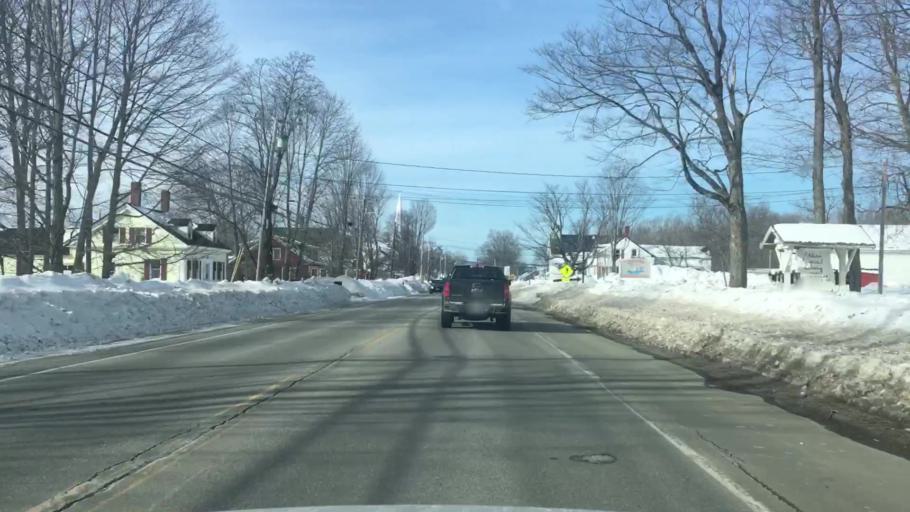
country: US
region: Maine
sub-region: Penobscot County
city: Charleston
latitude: 45.0001
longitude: -69.0217
